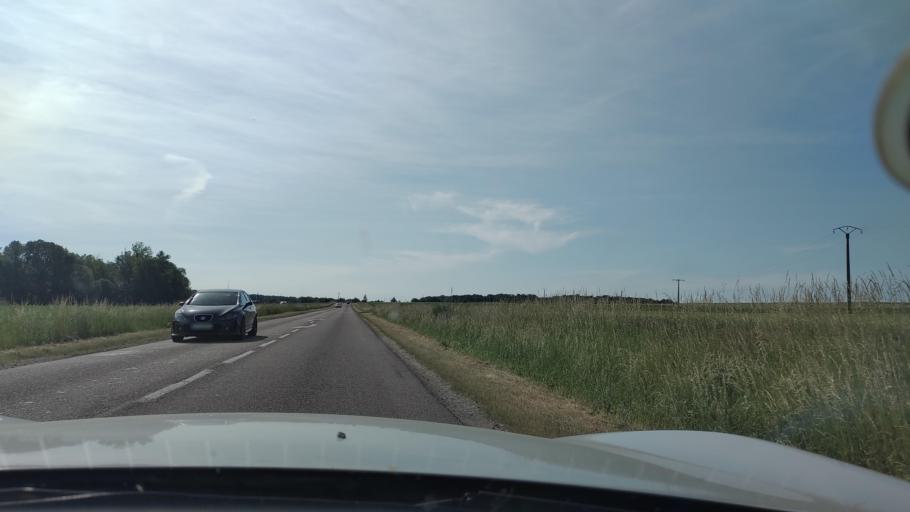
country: FR
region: Champagne-Ardenne
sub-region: Departement de l'Aube
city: Nogent-sur-Seine
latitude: 48.4823
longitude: 3.5402
